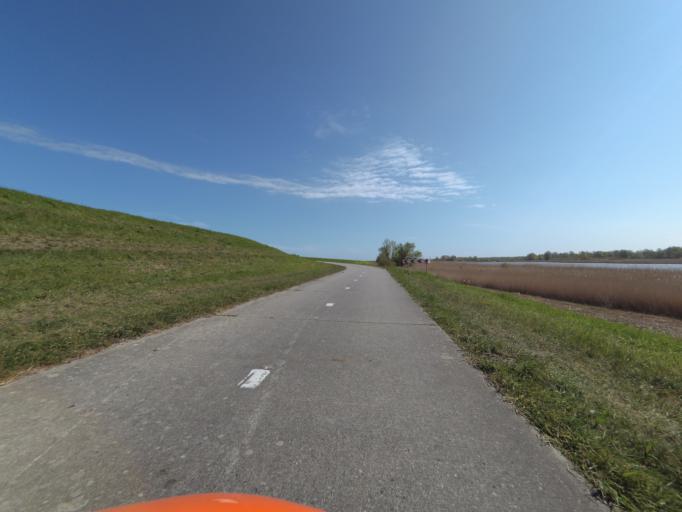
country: NL
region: Flevoland
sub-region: Gemeente Almere
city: Almere Stad
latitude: 52.4126
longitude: 5.1981
